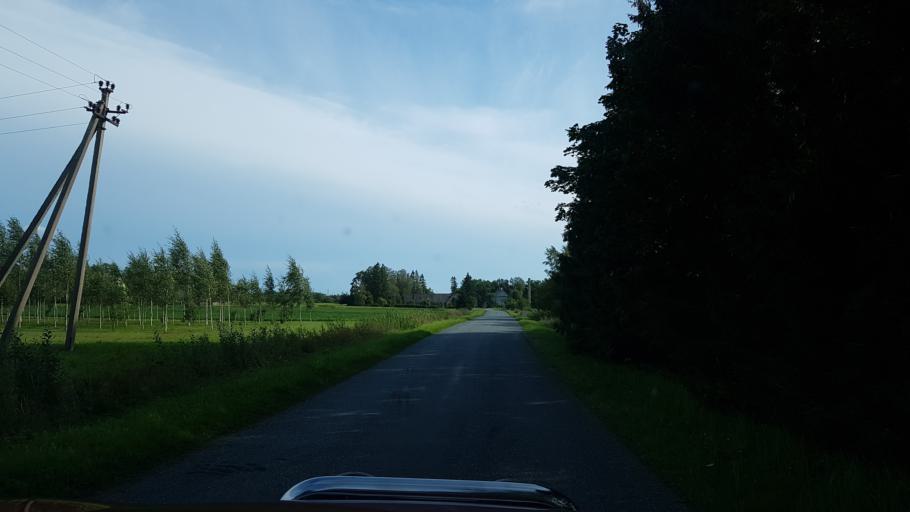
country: EE
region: Laeaene
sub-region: Lihula vald
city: Lihula
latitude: 58.4382
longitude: 24.0054
